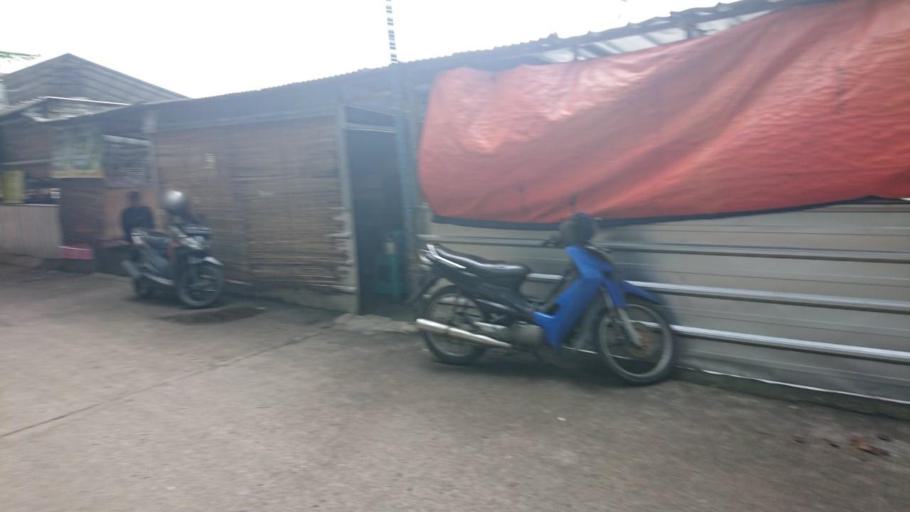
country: ID
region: West Java
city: Depok
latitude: -6.3361
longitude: 106.8850
